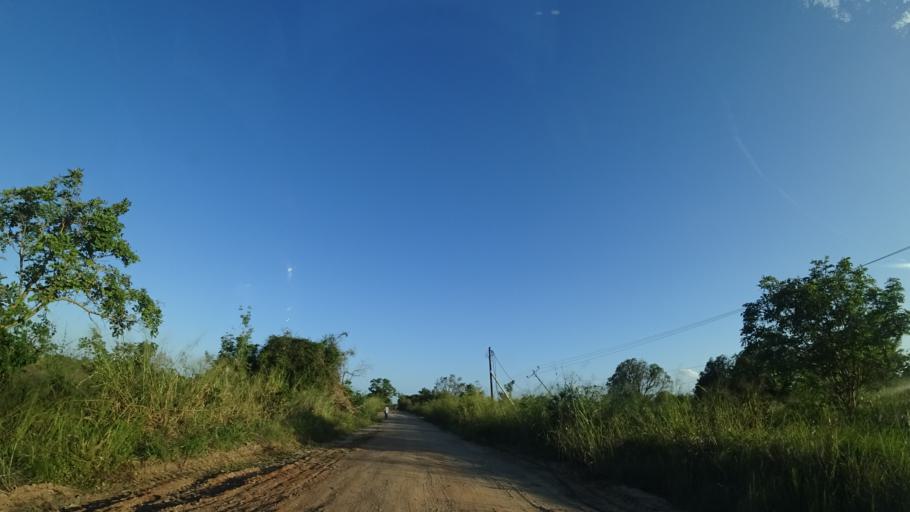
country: MZ
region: Sofala
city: Dondo
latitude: -19.3972
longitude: 34.7089
